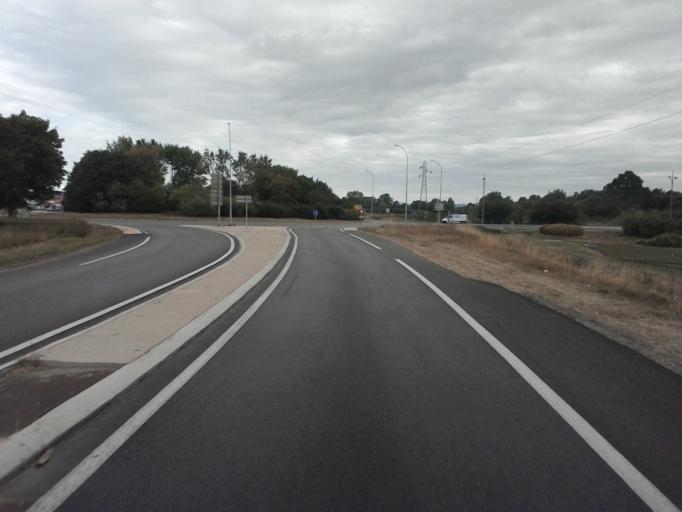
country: FR
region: Rhone-Alpes
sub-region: Departement de l'Ain
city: Amberieu-en-Bugey
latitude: 45.9820
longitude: 5.3481
